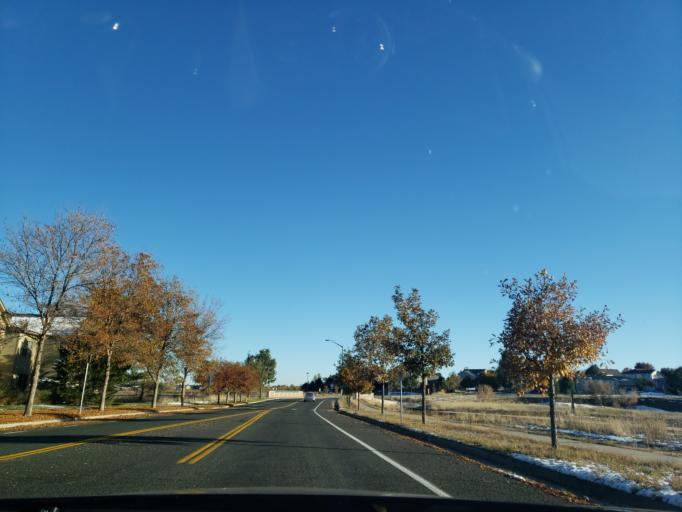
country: US
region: Colorado
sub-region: Larimer County
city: Fort Collins
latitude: 40.5083
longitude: -105.0676
